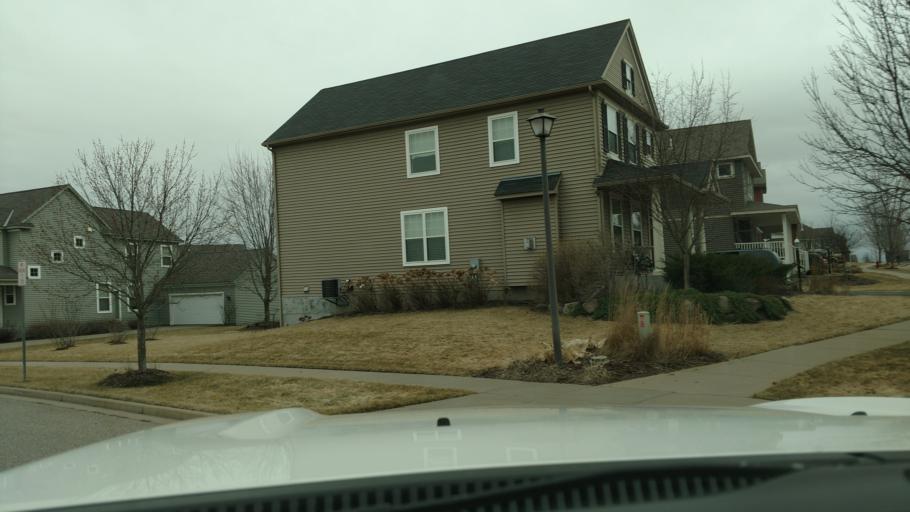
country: US
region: Wisconsin
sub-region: Saint Croix County
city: Hudson
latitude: 44.9571
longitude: -92.7000
